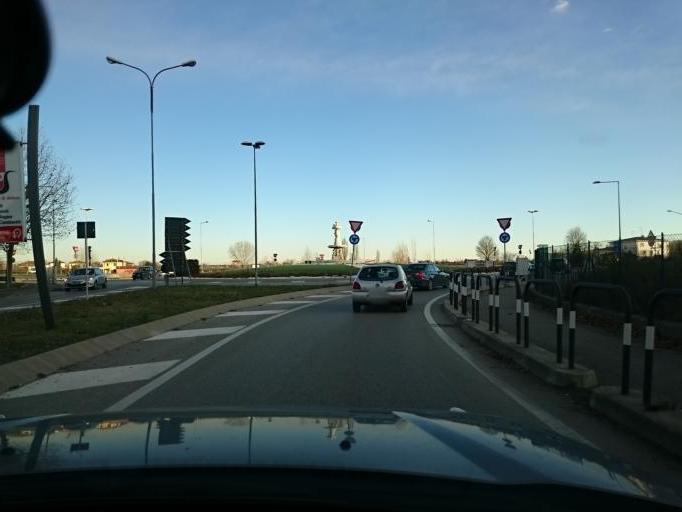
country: IT
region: Veneto
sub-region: Provincia di Padova
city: Montegrotto Terme
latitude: 45.3211
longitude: 11.7852
